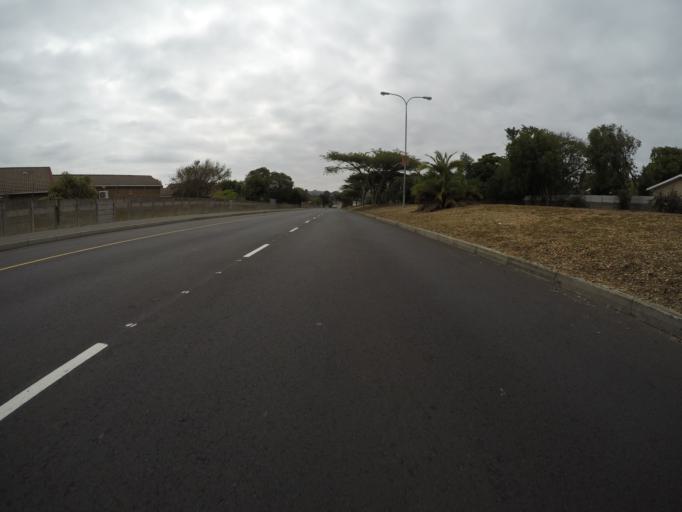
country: ZA
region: Western Cape
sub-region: City of Cape Town
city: Kraaifontein
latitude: -33.8665
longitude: 18.6330
